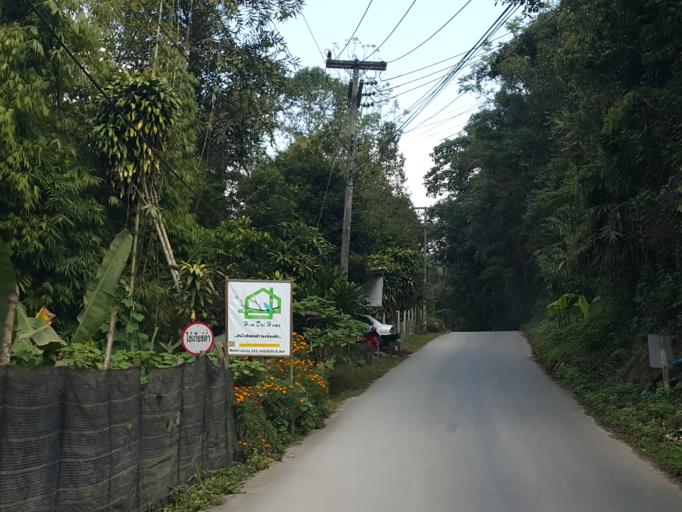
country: TH
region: Chiang Mai
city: Mae On
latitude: 18.8646
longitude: 99.3402
